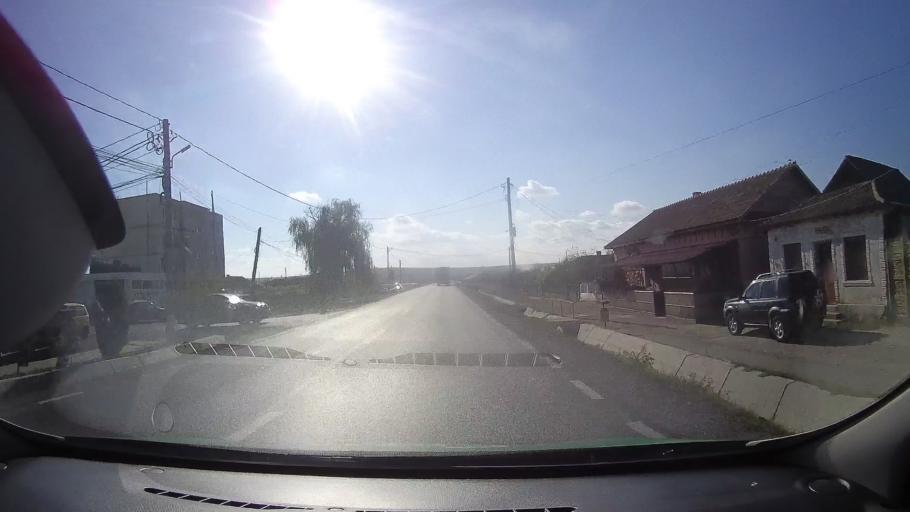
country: RO
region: Tulcea
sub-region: Comuna Baia
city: Baia
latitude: 44.7251
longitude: 28.6801
